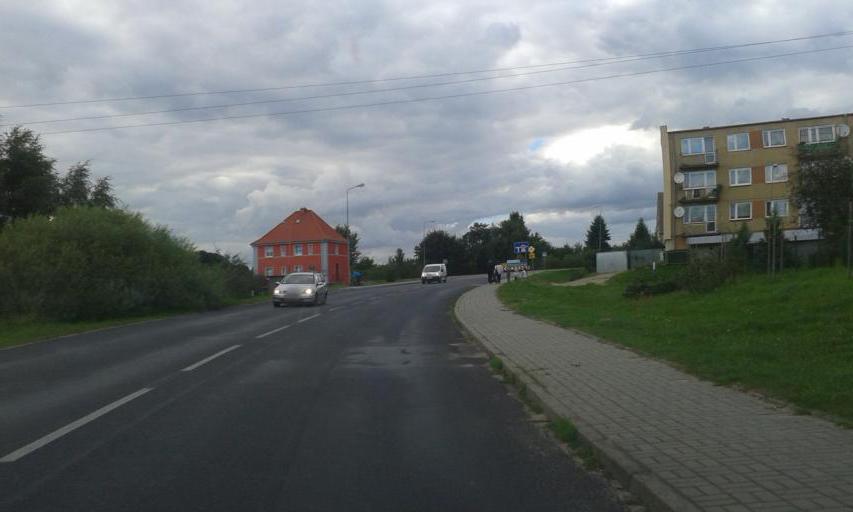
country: PL
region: West Pomeranian Voivodeship
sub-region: Powiat szczecinecki
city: Barwice
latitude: 53.7436
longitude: 16.3493
